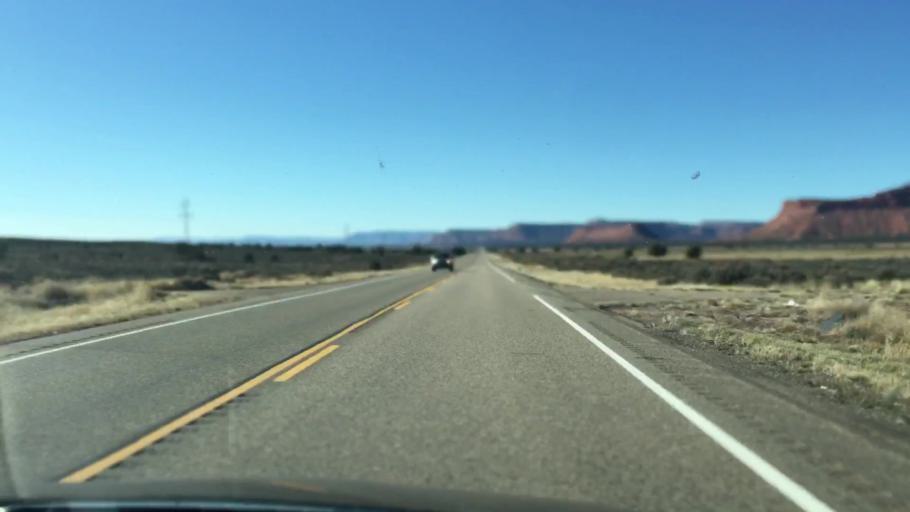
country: US
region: Utah
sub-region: Kane County
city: Kanab
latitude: 37.0395
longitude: -112.2879
